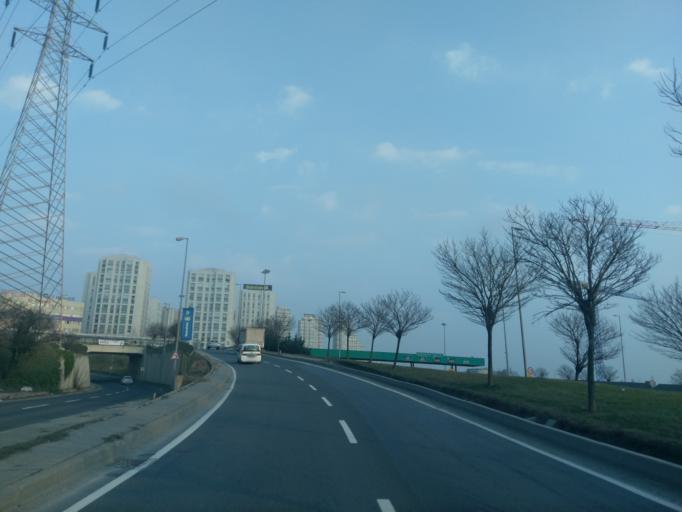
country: TR
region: Istanbul
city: Esenyurt
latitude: 41.0594
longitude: 28.7079
